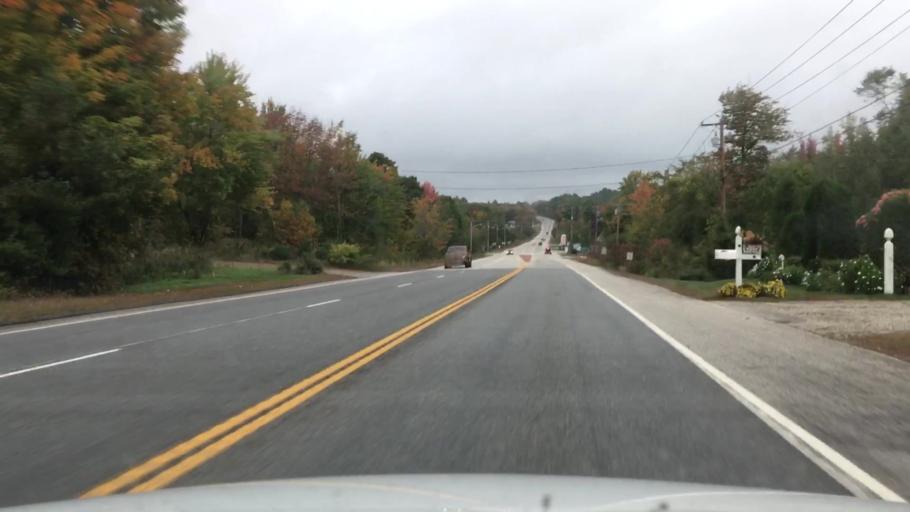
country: US
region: Maine
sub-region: Androscoggin County
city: Poland
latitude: 44.0107
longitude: -70.3623
